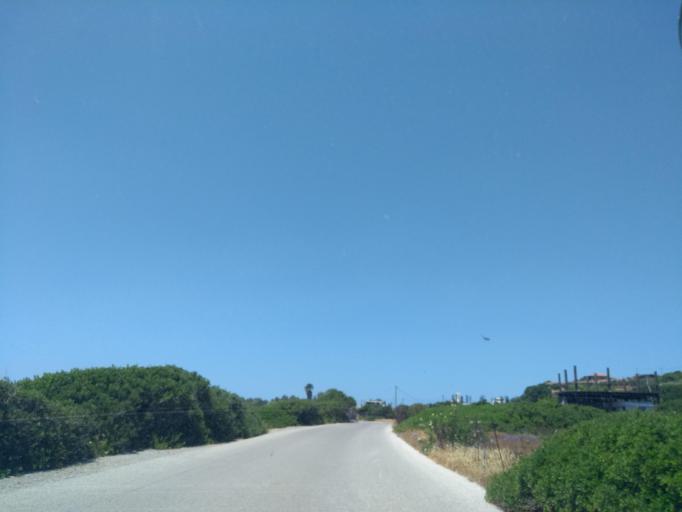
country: GR
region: Crete
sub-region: Nomos Chanias
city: Vryses
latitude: 35.3576
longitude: 23.5323
